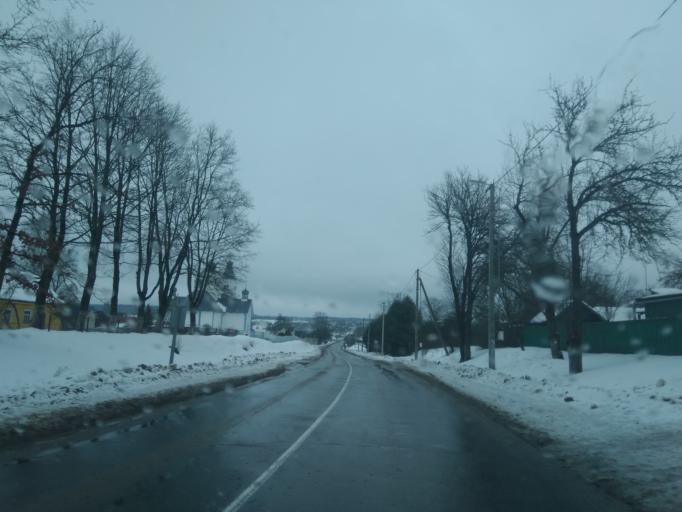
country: BY
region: Minsk
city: Stowbtsy
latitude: 53.5795
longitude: 26.8303
